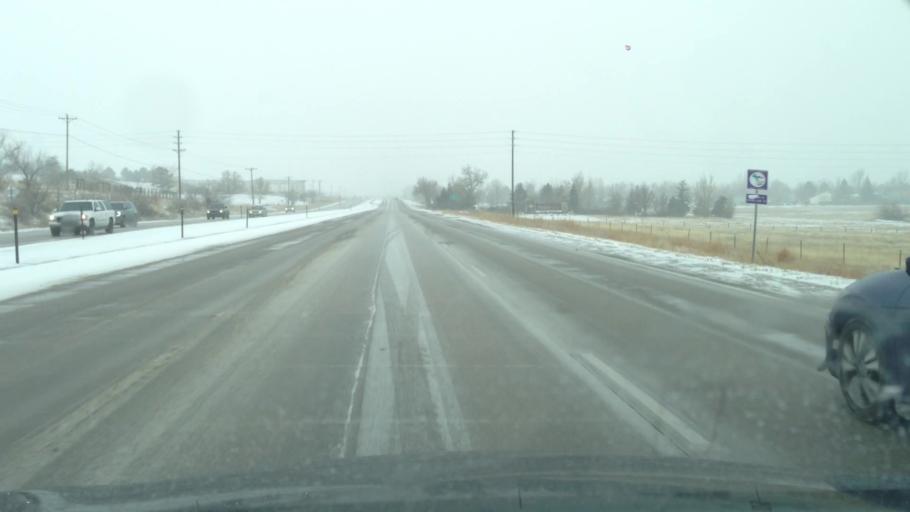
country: US
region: Colorado
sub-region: Douglas County
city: Stonegate
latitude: 39.5674
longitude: -104.7861
